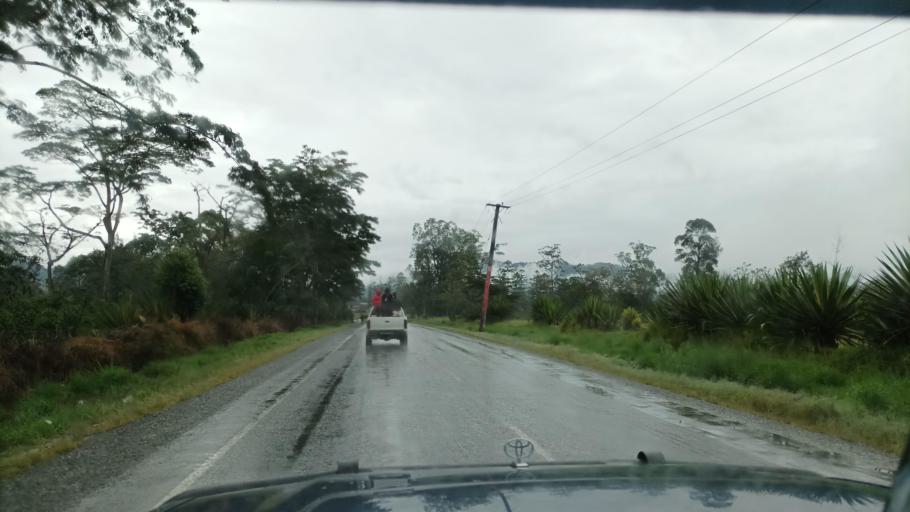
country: PG
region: Western Highlands
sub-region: Hagen
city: Mount Hagen
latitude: -5.8391
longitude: 144.3210
